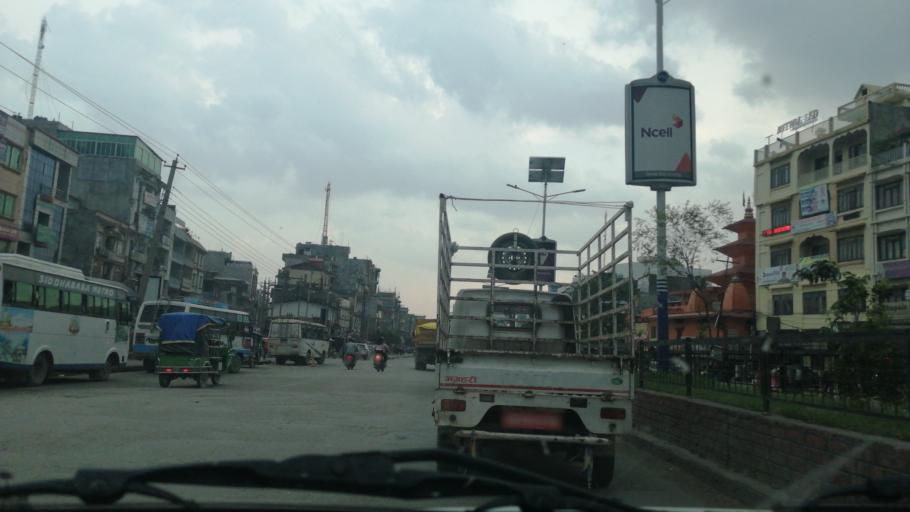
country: NP
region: Western Region
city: Butwal
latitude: 27.7012
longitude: 83.4661
